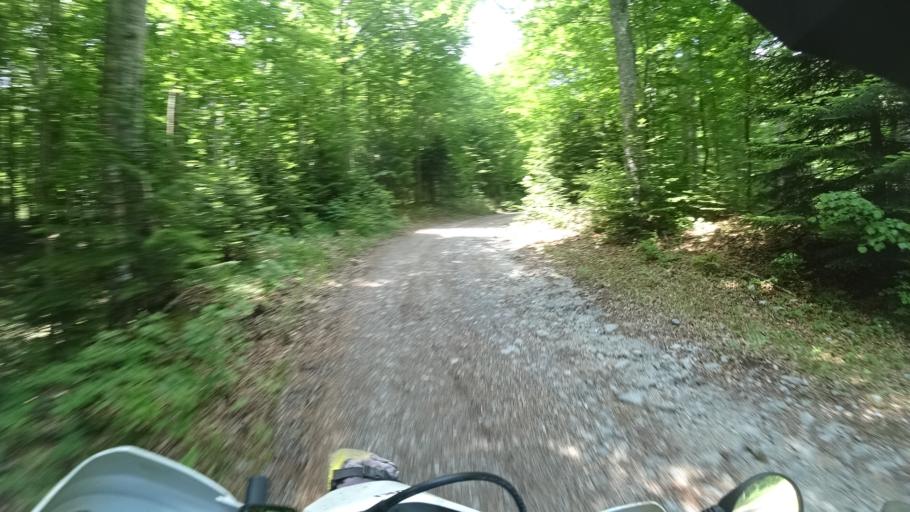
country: HR
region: Zadarska
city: Gracac
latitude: 44.4915
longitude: 15.8758
